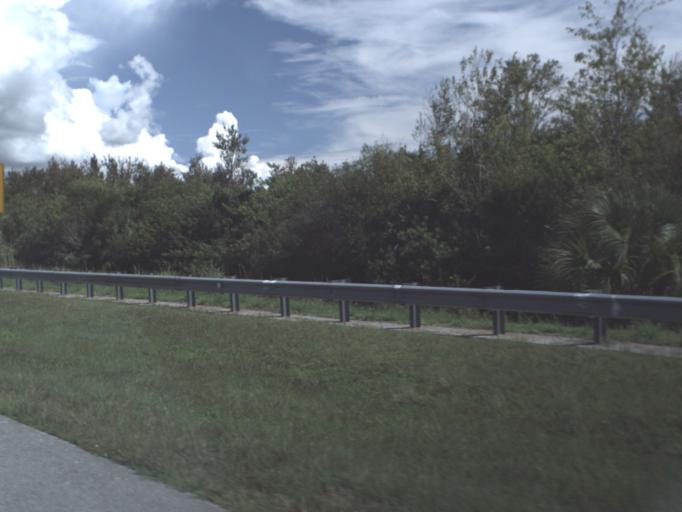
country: US
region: Florida
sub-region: Collier County
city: Lely Resort
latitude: 25.9678
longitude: -81.3528
